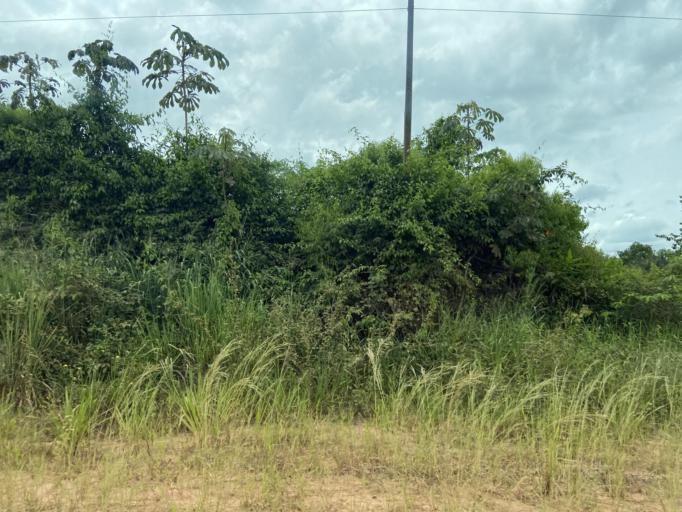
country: BR
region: Para
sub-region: Maraba
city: Maraba
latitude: -5.2534
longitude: -48.9778
